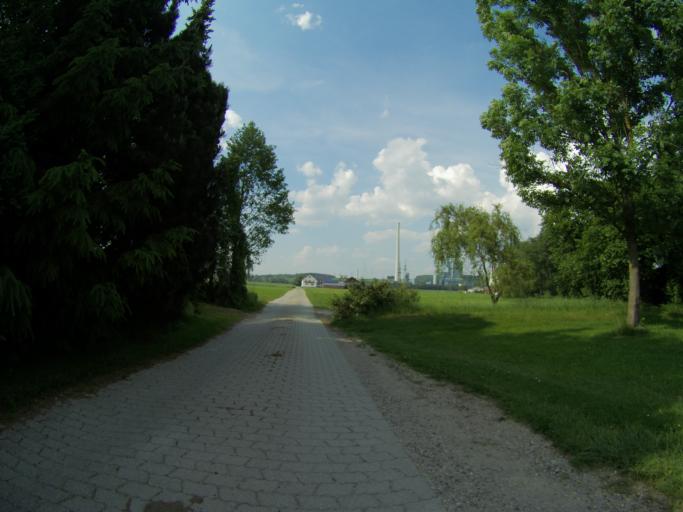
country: DE
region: Bavaria
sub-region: Upper Bavaria
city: Haag an der Amper
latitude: 48.4452
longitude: 11.7993
